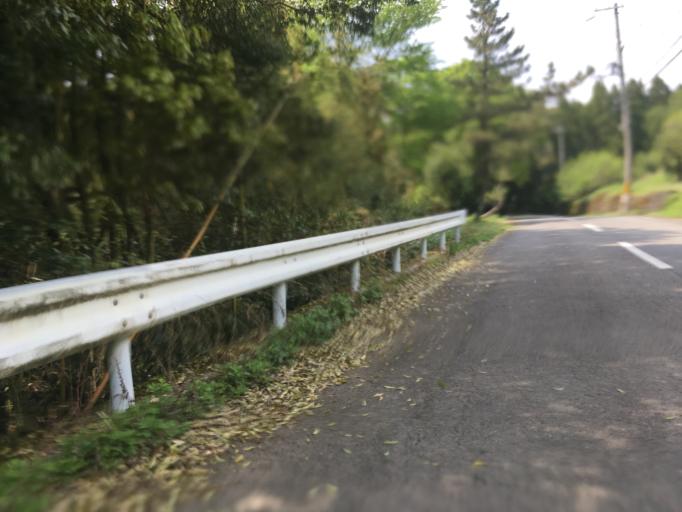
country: JP
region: Kyoto
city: Kameoka
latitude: 35.0864
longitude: 135.6114
